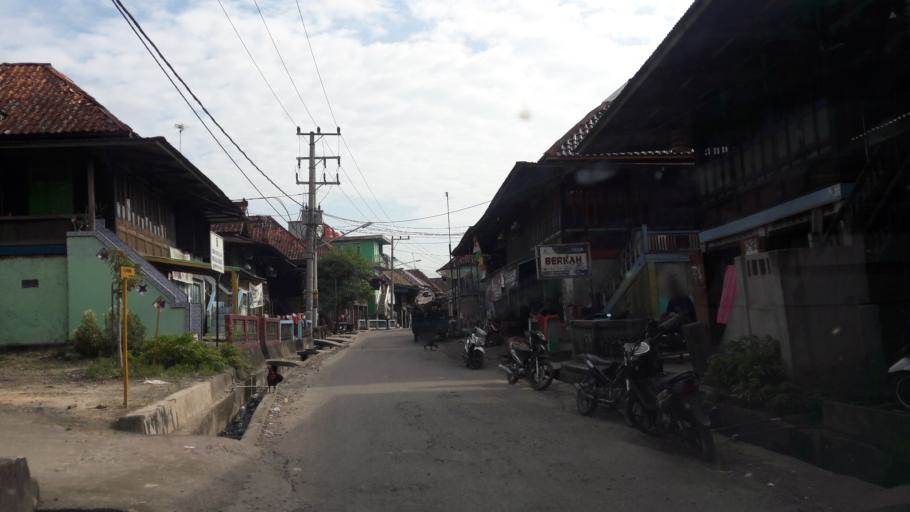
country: ID
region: South Sumatra
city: Gunungmenang
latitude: -3.0899
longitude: 104.0217
